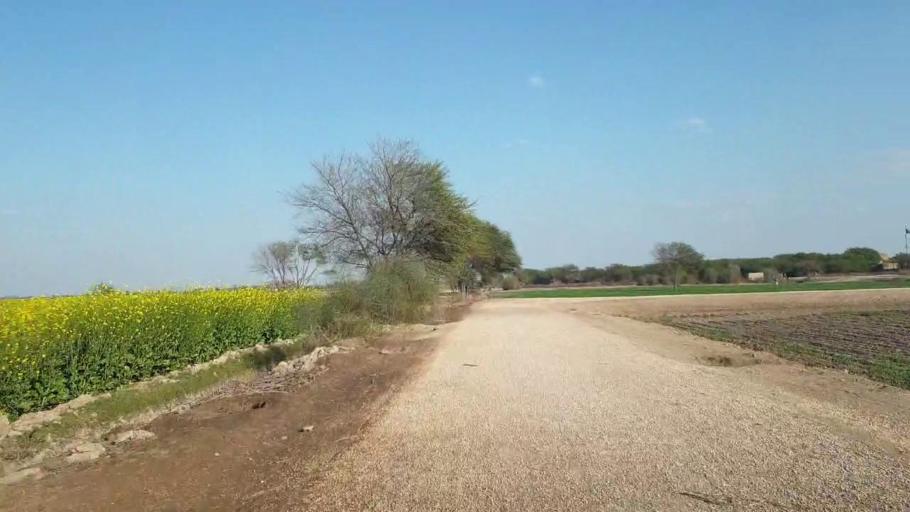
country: PK
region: Sindh
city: Shahpur Chakar
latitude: 26.1196
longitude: 68.5750
